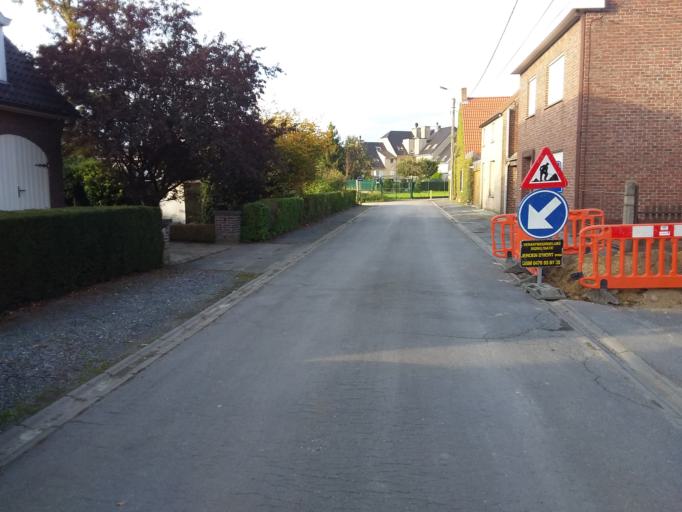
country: BE
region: Flanders
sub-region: Provincie Oost-Vlaanderen
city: Zulte
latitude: 50.9344
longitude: 3.4655
